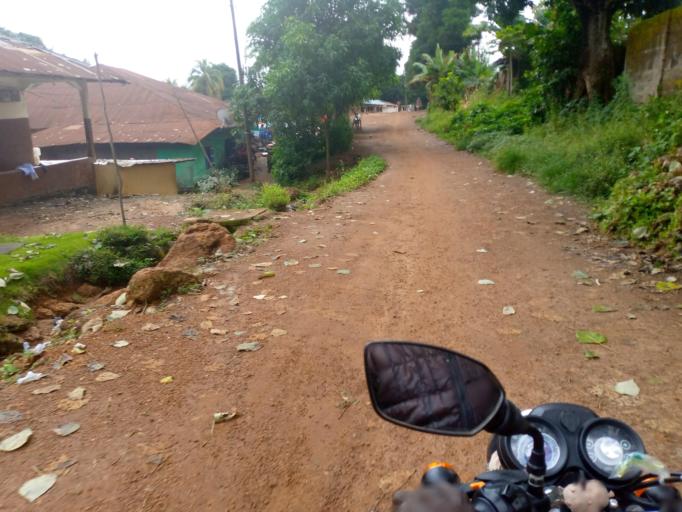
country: SL
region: Eastern Province
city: Kenema
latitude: 7.8776
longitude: -11.1833
